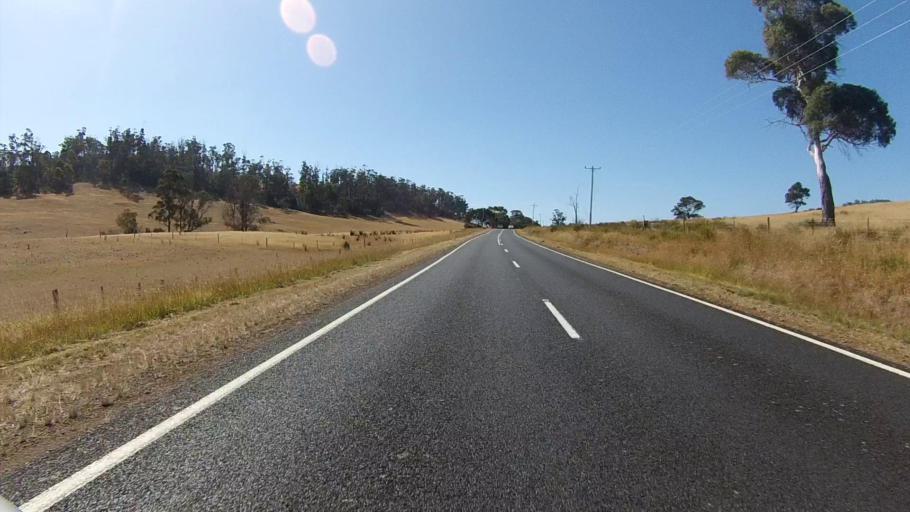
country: AU
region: Tasmania
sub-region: Sorell
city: Sorell
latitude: -42.4295
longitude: 147.9318
